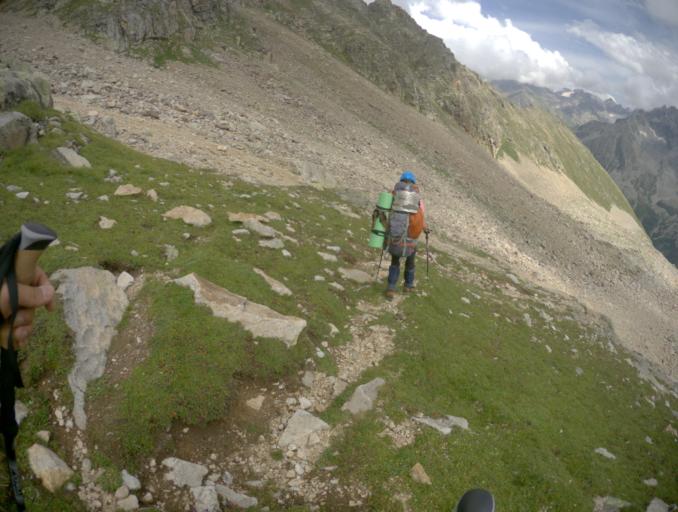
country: RU
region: Karachayevo-Cherkesiya
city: Uchkulan
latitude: 43.2755
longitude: 42.1218
